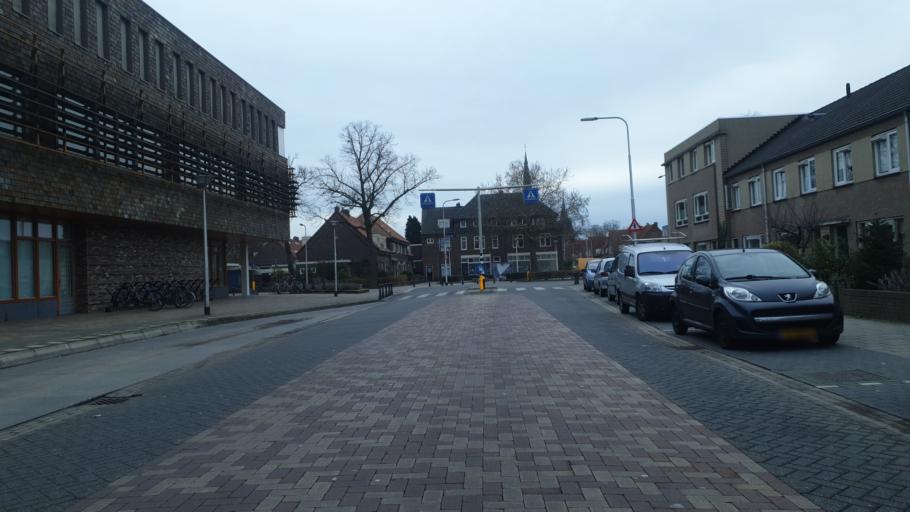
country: NL
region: Gelderland
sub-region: Gemeente Nijmegen
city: Nijmegen
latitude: 51.8337
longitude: 5.8488
